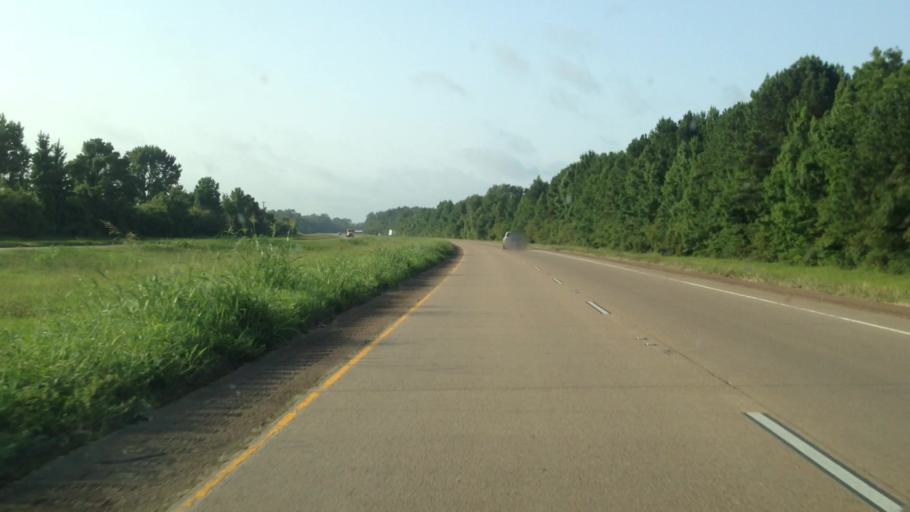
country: US
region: Louisiana
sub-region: Rapides Parish
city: Woodworth
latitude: 31.1414
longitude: -92.4516
